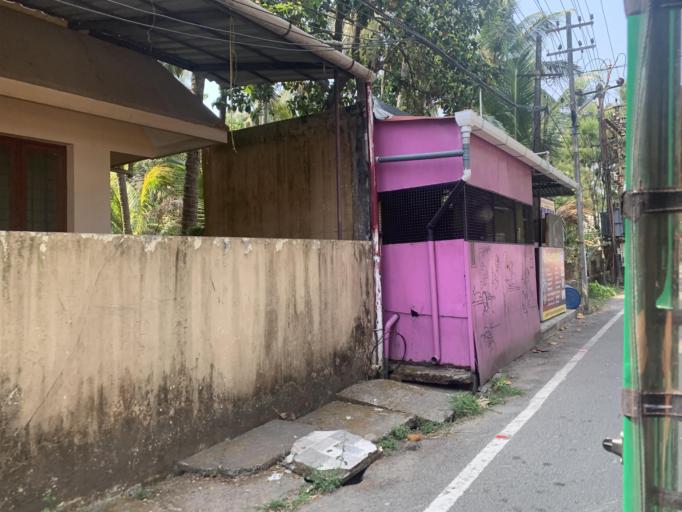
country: IN
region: Kerala
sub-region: Ernakulam
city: Cochin
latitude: 9.9411
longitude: 76.3016
